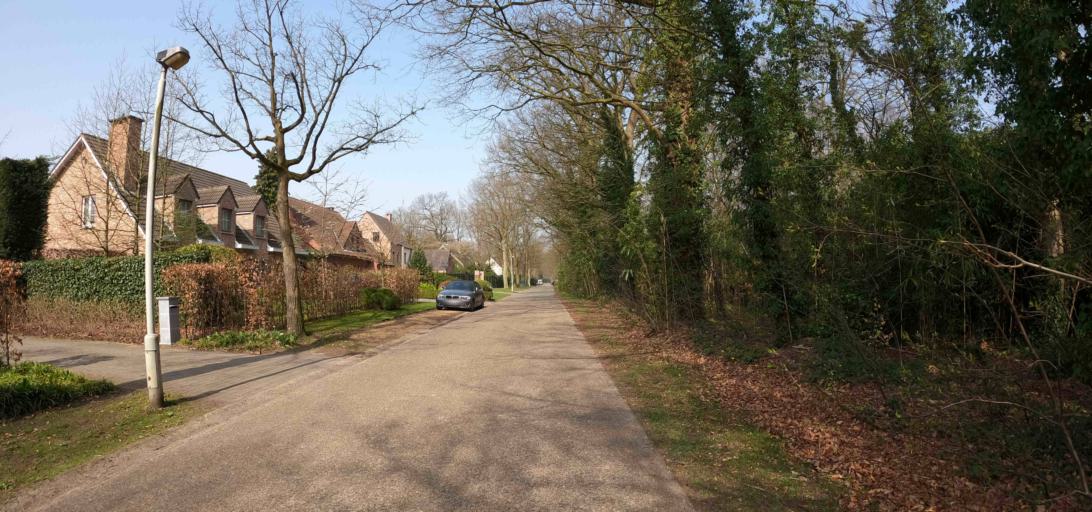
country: BE
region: Flanders
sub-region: Provincie Antwerpen
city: Kapellen
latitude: 51.3265
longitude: 4.4230
